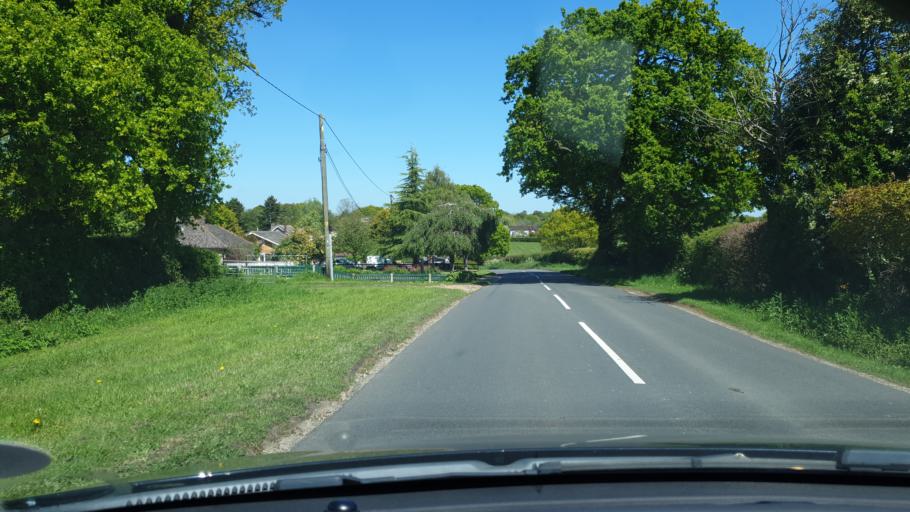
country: GB
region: England
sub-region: Essex
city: Little Clacton
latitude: 51.8613
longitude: 1.1196
